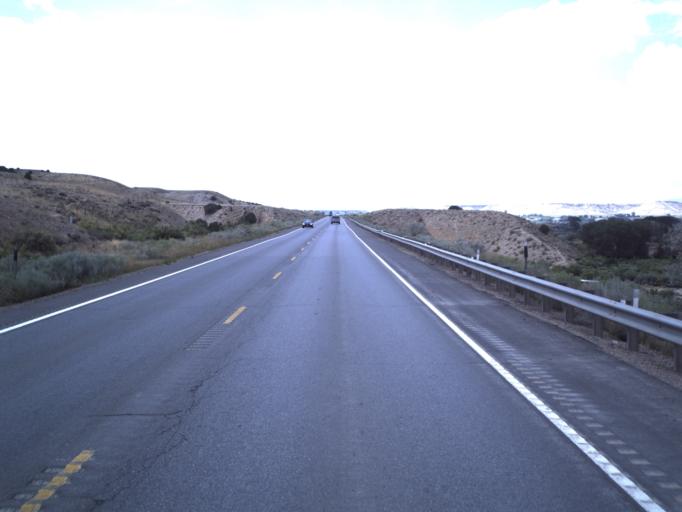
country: US
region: Utah
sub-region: Duchesne County
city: Duchesne
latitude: 40.1628
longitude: -110.2781
